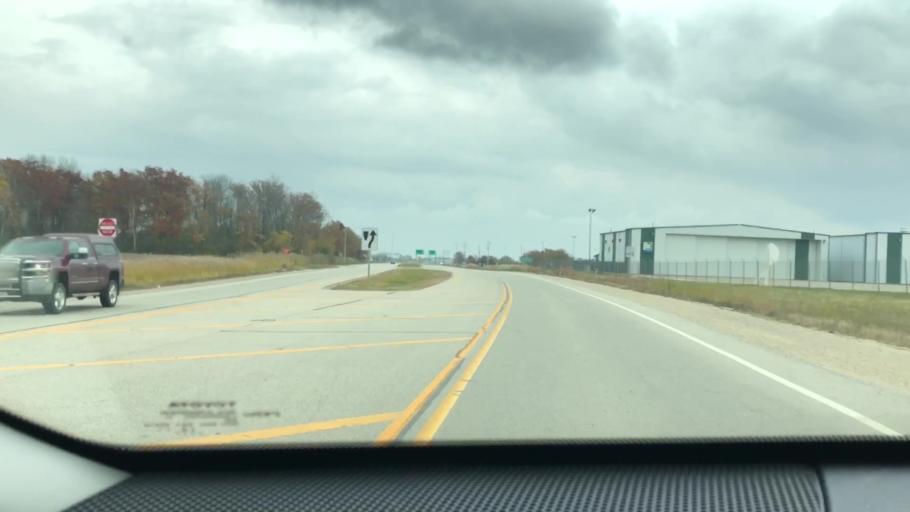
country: US
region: Wisconsin
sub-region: Brown County
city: Oneida
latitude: 44.4957
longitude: -88.1321
